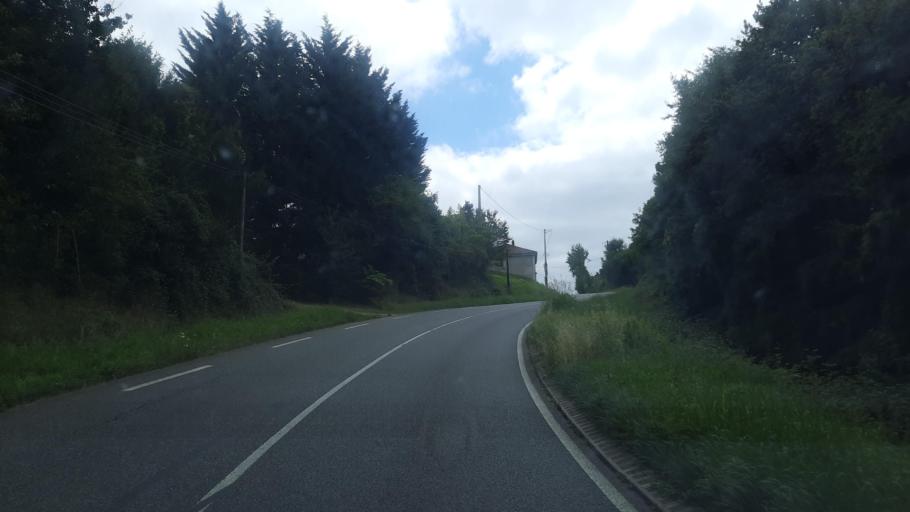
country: FR
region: Midi-Pyrenees
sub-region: Departement des Hautes-Pyrenees
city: Trie-sur-Baise
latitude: 43.3085
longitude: 0.3797
